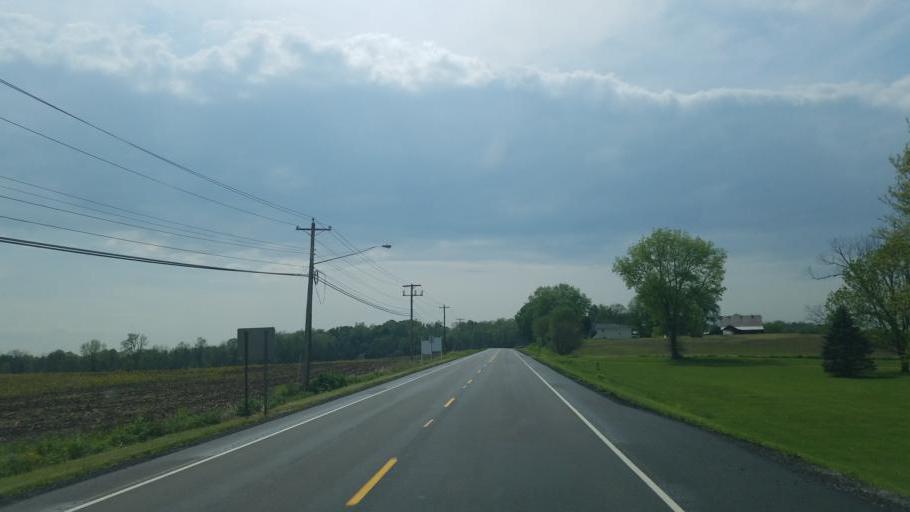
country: US
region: Ohio
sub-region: Licking County
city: Hebron
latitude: 39.9588
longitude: -82.5102
